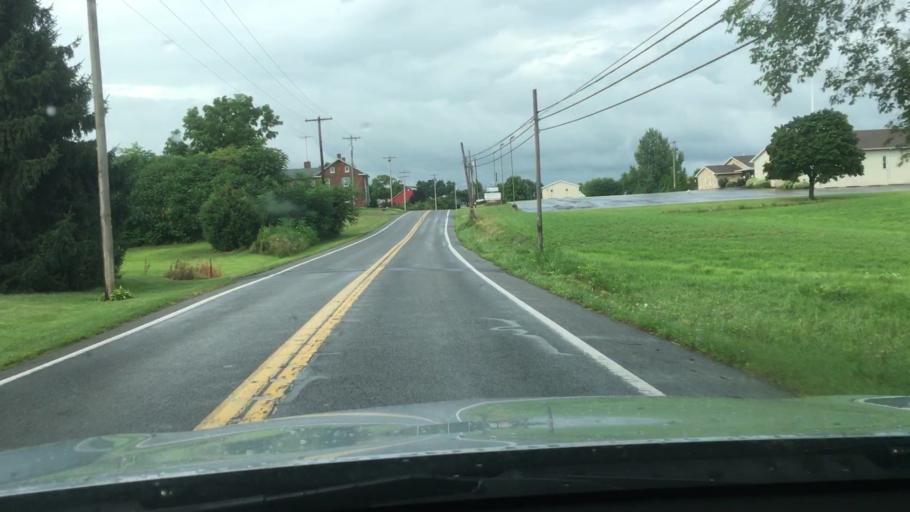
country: US
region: Pennsylvania
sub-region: Franklin County
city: Chambersburg
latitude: 39.9027
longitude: -77.7179
